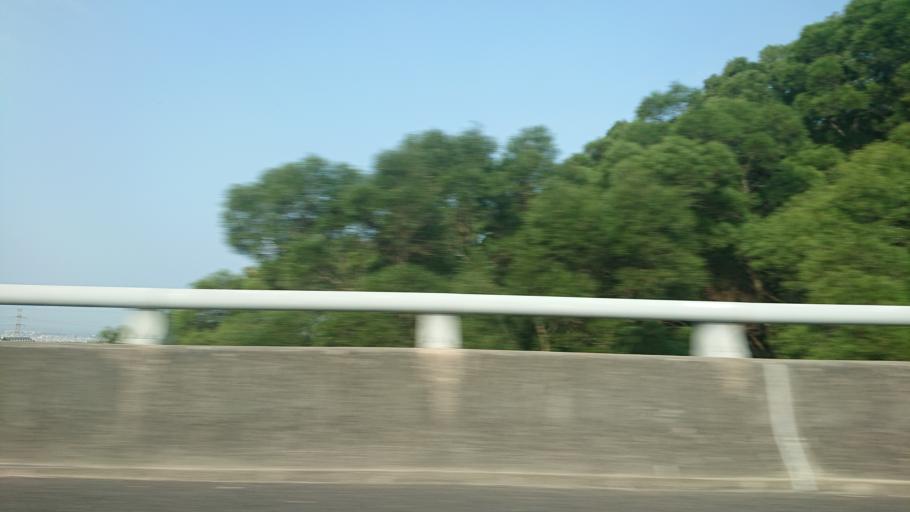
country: TW
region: Taiwan
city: Fengyuan
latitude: 24.2673
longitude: 120.5899
